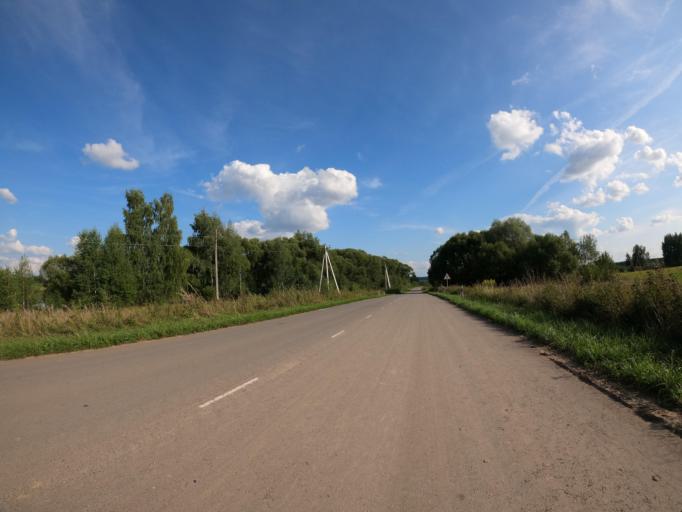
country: RU
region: Moskovskaya
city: Troitskoye
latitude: 55.2099
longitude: 38.4874
